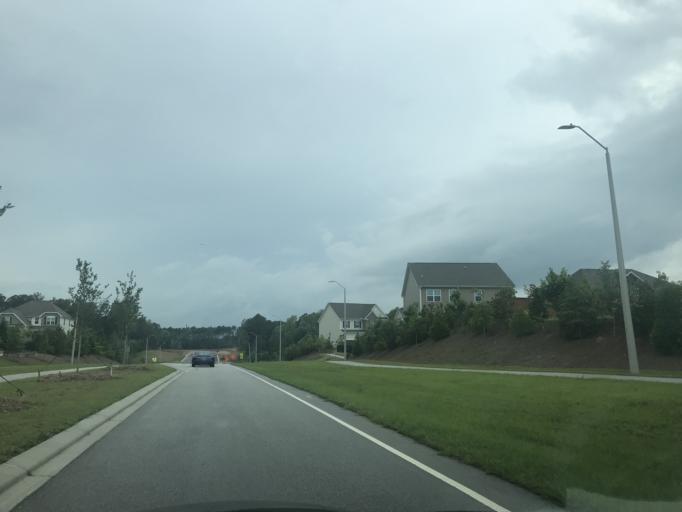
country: US
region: North Carolina
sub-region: Wake County
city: Green Level
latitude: 35.8107
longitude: -78.8840
